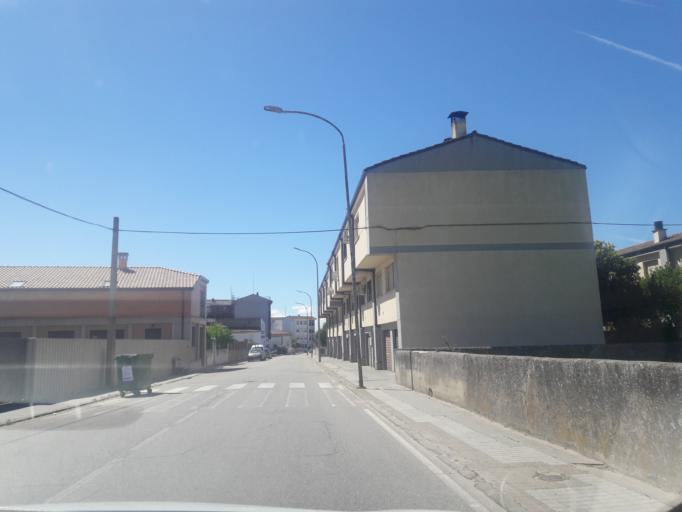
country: ES
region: Castille and Leon
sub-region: Provincia de Salamanca
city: Vitigudino
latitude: 41.0082
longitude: -6.4375
